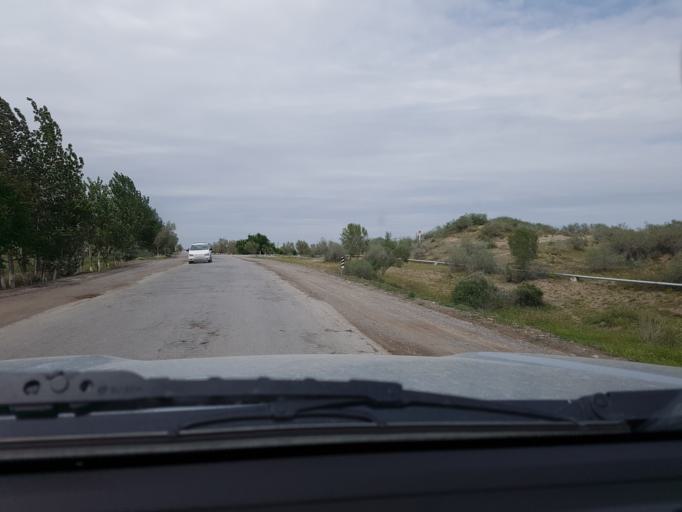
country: TM
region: Lebap
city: Atamyrat
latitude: 38.1130
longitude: 64.7346
